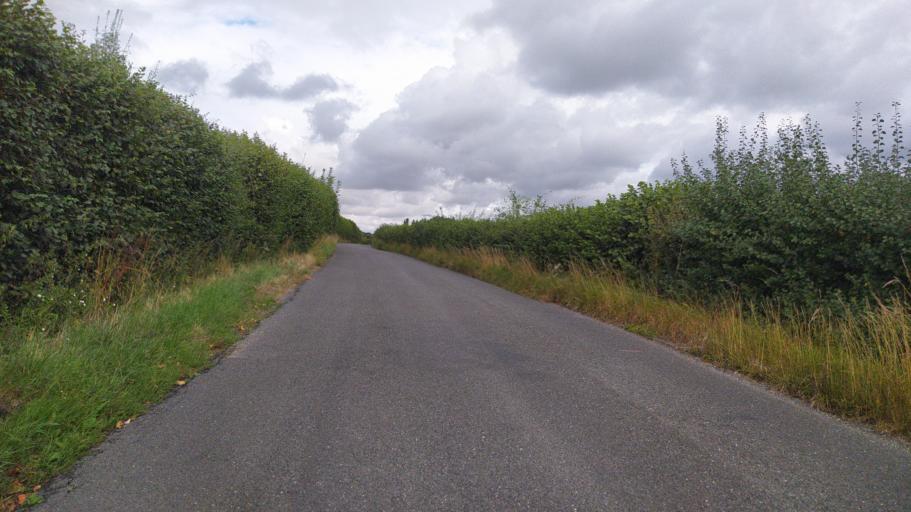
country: GB
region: England
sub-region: Hampshire
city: Petersfield
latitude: 50.9794
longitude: -0.9529
